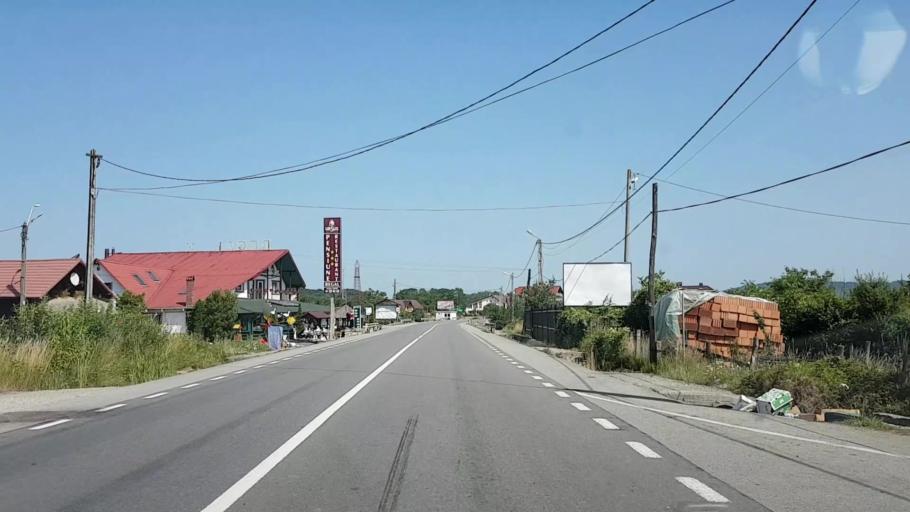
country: RO
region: Bistrita-Nasaud
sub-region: Comuna Uriu
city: Cristestii Ciceului
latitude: 47.1825
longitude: 24.1349
